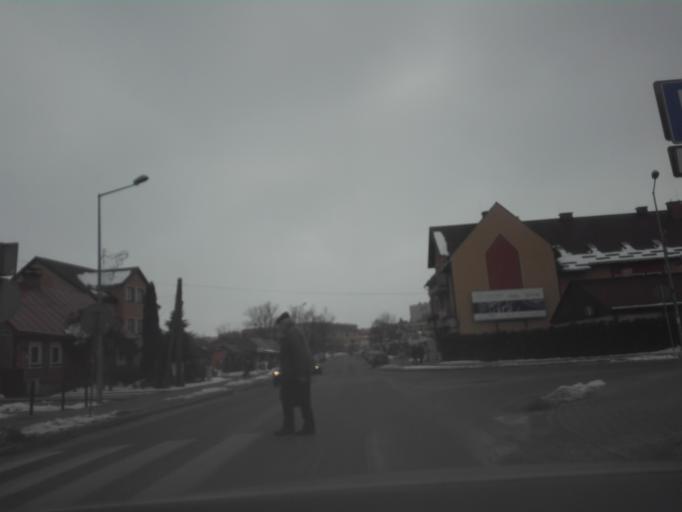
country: PL
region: Lublin Voivodeship
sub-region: Powiat hrubieszowski
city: Hrubieszow
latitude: 50.8051
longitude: 23.8944
